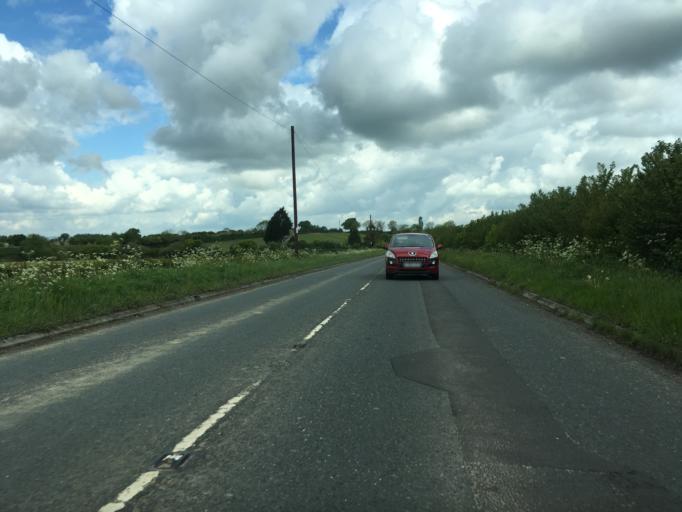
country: GB
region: England
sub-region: Gloucestershire
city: Stonehouse
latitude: 51.7582
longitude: -2.2835
